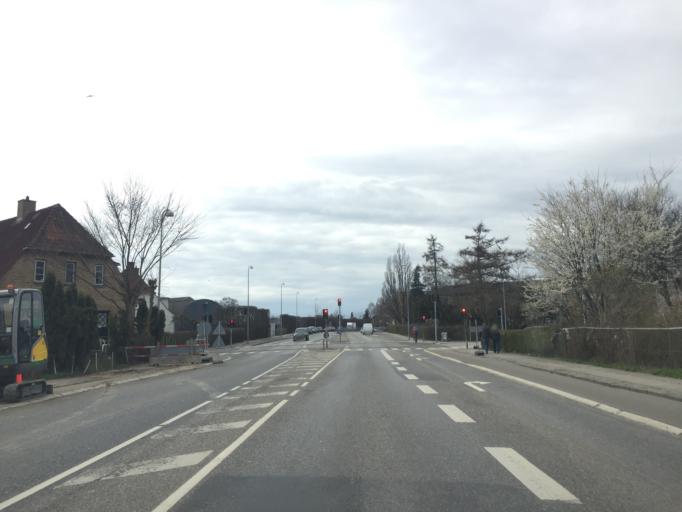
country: DK
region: Capital Region
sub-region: Lyngby-Tarbaek Kommune
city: Kongens Lyngby
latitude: 55.7667
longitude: 12.4948
